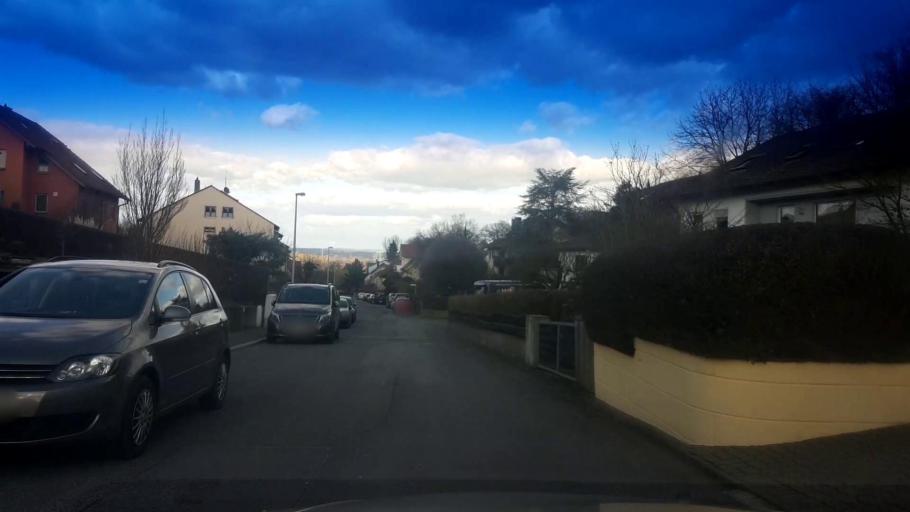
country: DE
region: Bavaria
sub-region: Upper Franconia
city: Bischberg
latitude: 49.9058
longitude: 10.8305
